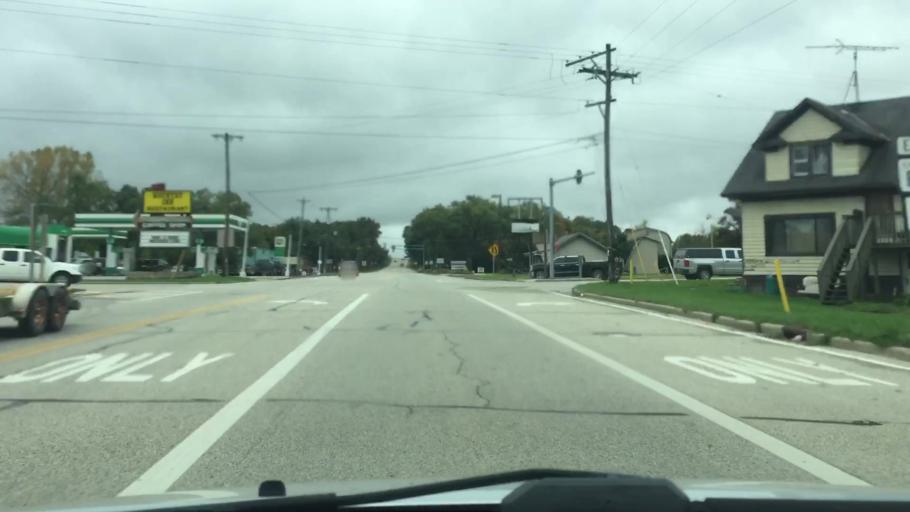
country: US
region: Wisconsin
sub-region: Walworth County
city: Elkhorn
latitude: 42.7260
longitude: -88.5428
